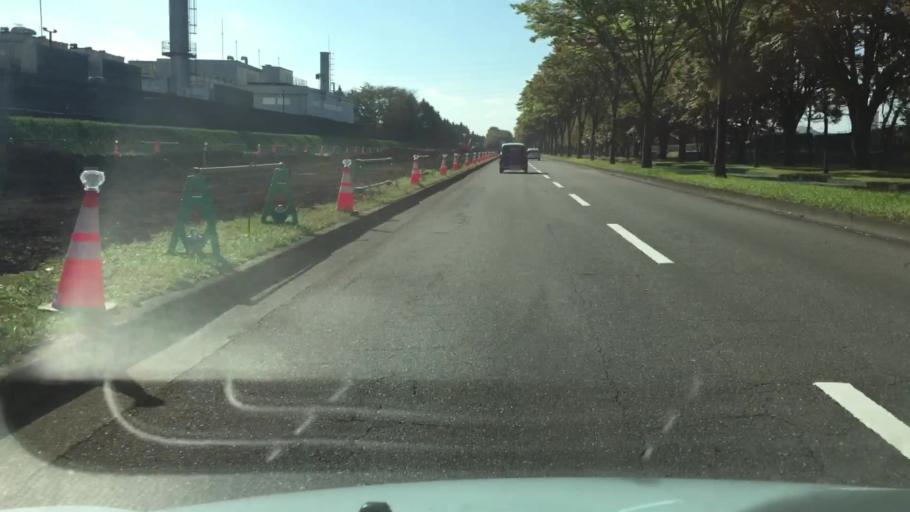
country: JP
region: Tochigi
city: Utsunomiya-shi
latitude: 36.5525
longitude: 139.9834
